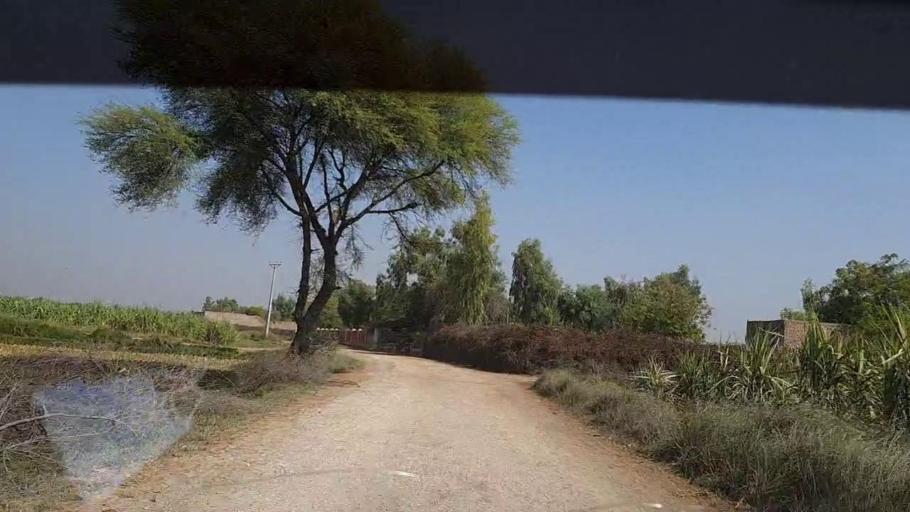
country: PK
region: Sindh
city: Naudero
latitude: 27.6469
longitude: 68.3658
